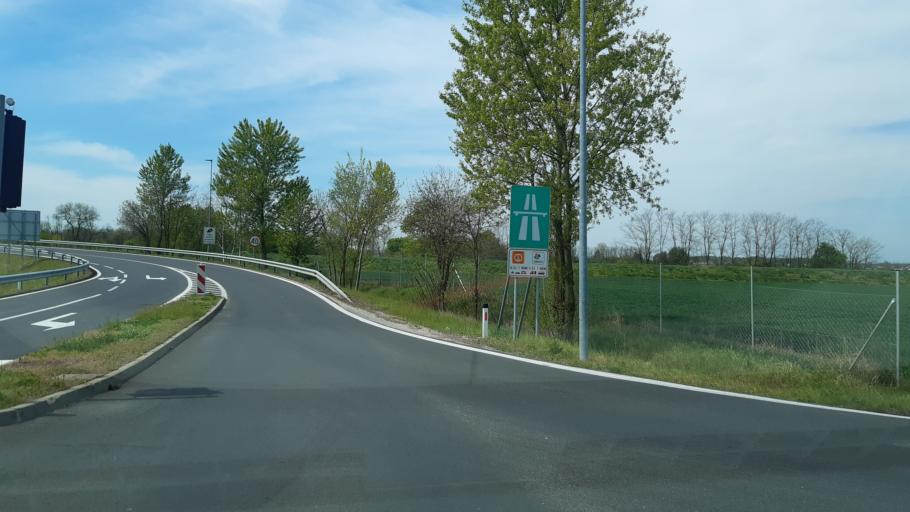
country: SI
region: Murska Sobota
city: Krog
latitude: 46.6359
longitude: 16.1572
